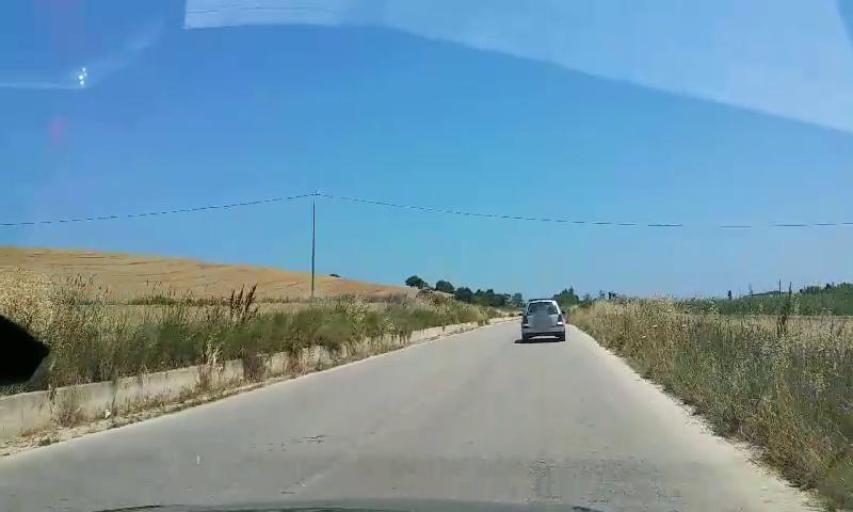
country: IT
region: Molise
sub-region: Provincia di Campobasso
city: Termoli
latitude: 42.0002
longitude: 14.9570
